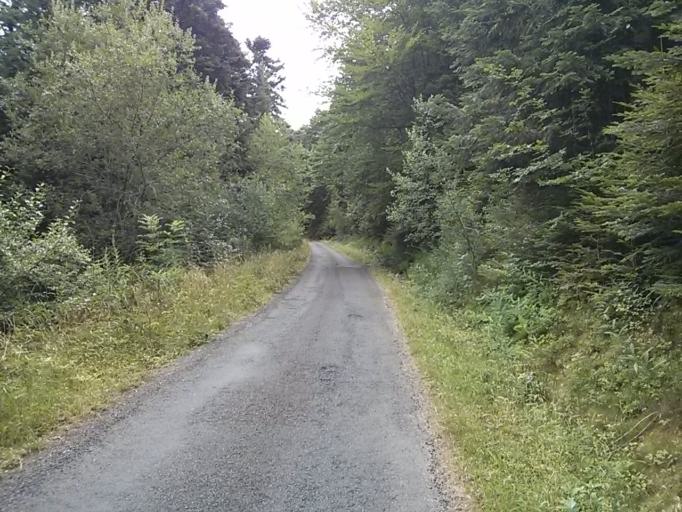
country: FR
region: Auvergne
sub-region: Departement de la Haute-Loire
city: Rosieres
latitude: 45.1066
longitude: 4.0449
